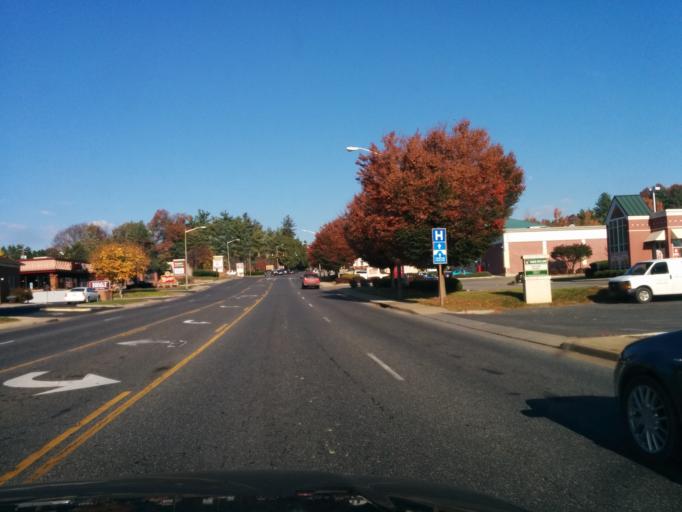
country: US
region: Virginia
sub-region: City of Lexington
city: Lexington
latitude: 37.7788
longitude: -79.4355
